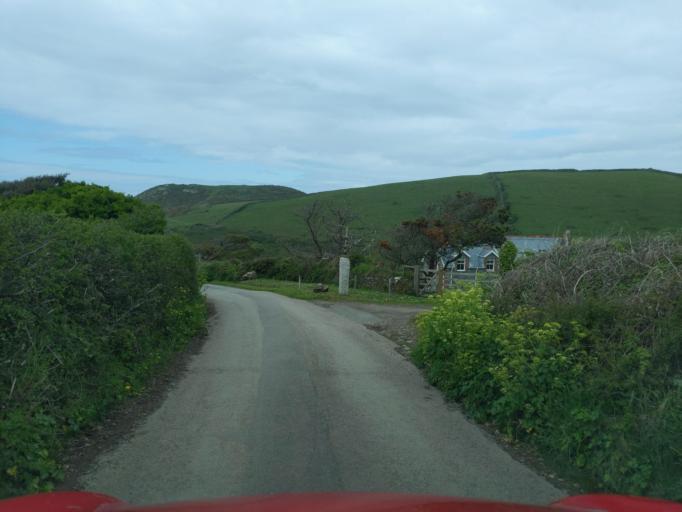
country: GB
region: England
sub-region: Cornwall
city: Polzeath
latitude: 50.5881
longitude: -4.8695
